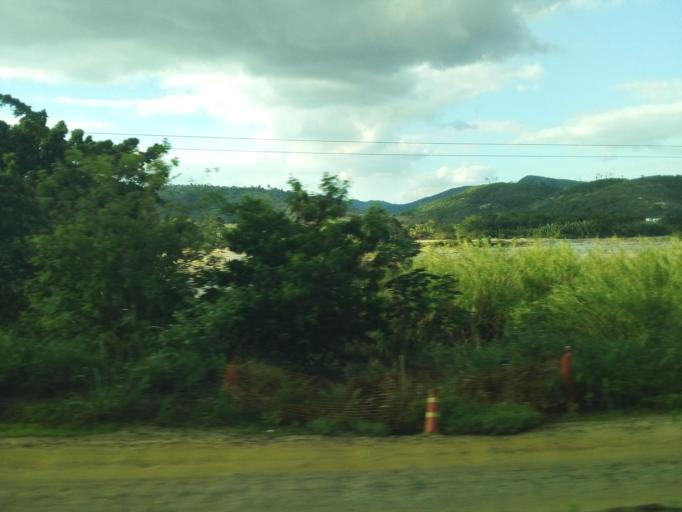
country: BR
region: Minas Gerais
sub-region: Resplendor
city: Resplendor
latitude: -19.2356
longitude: -41.3243
